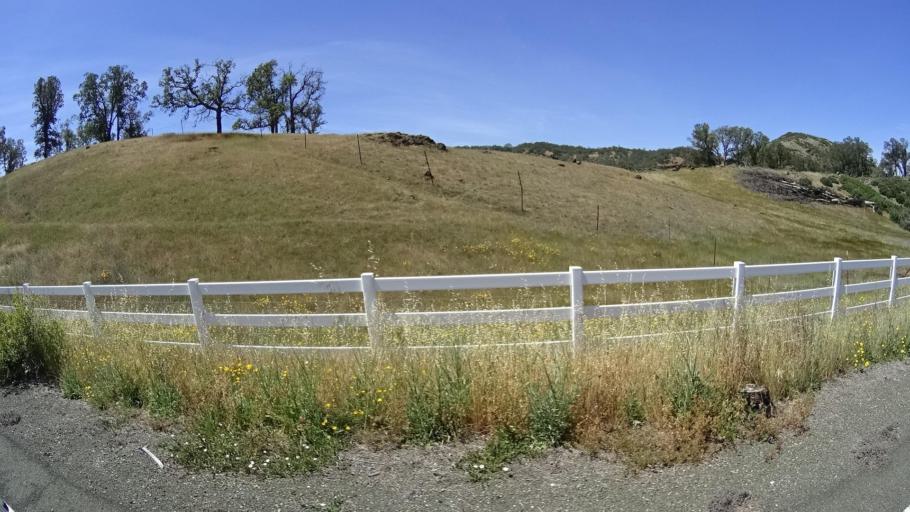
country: US
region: California
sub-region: Lake County
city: Hidden Valley Lake
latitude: 38.7279
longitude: -122.5177
